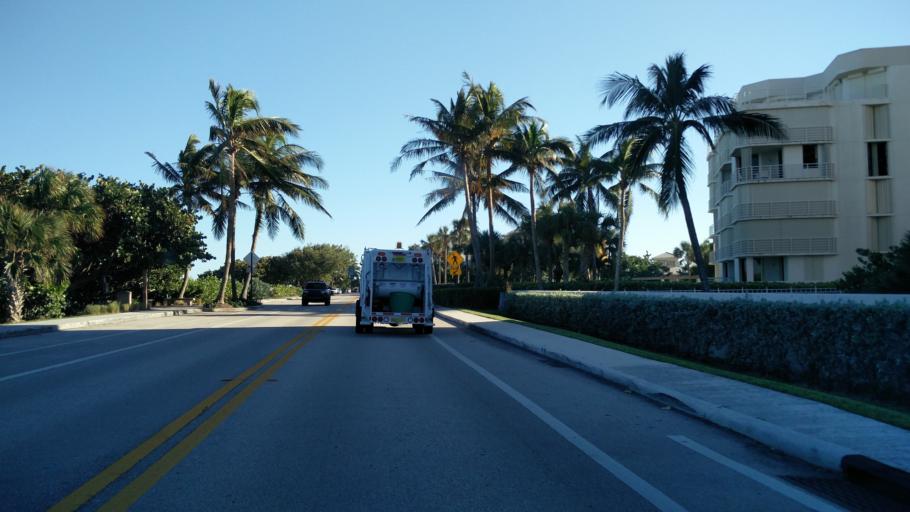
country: US
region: Florida
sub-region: Palm Beach County
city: Jupiter
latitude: 26.9180
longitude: -80.0654
